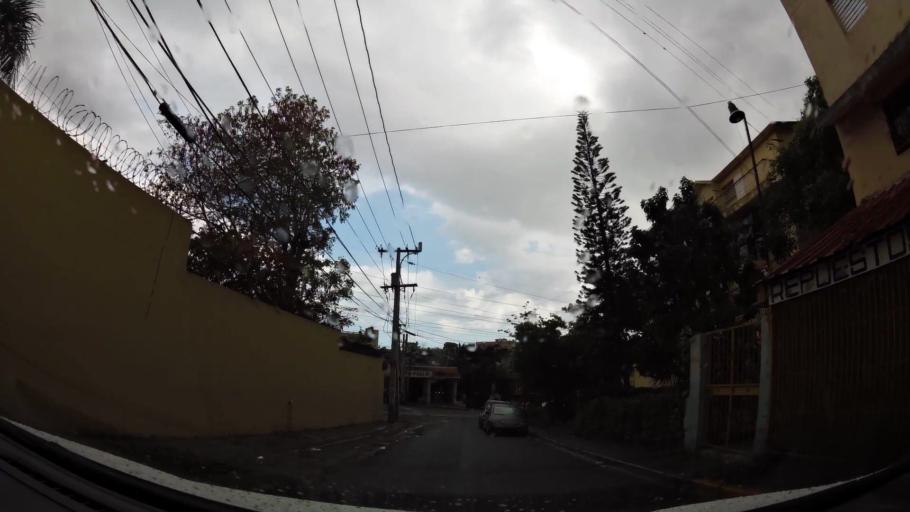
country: DO
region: Nacional
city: La Agustina
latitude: 18.4991
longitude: -69.9297
